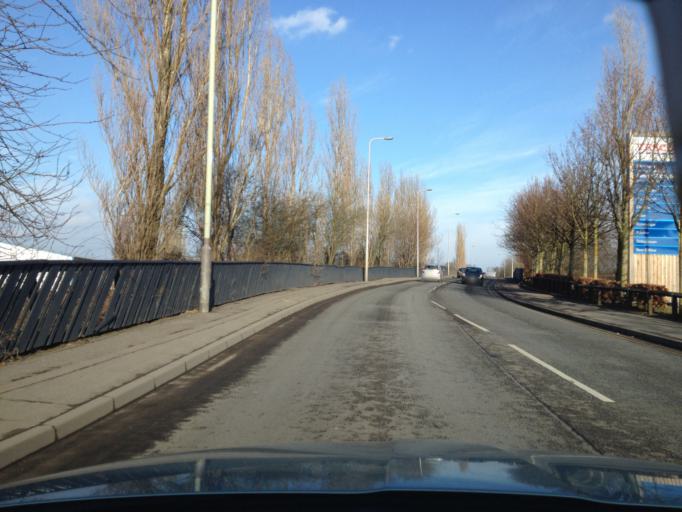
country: GB
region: Scotland
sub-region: Perth and Kinross
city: Perth
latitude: 56.3823
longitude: -3.4344
